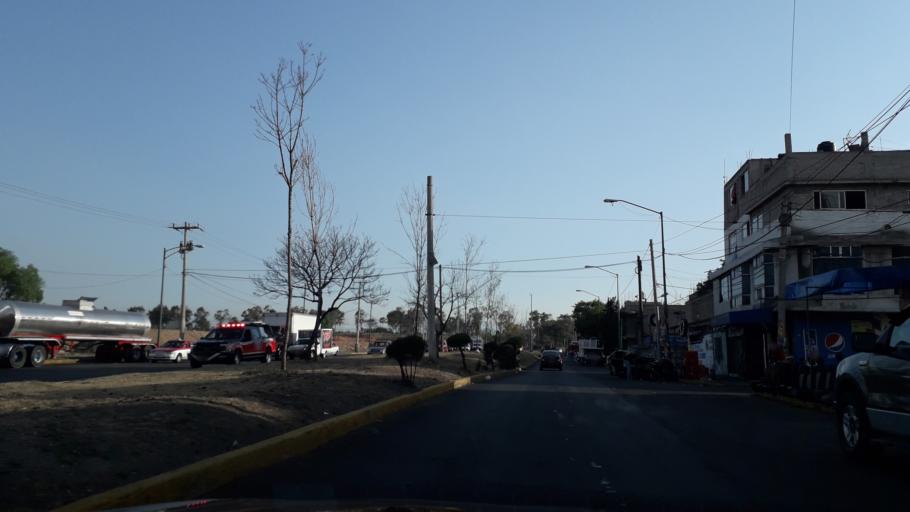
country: MX
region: Mexico City
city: Iztapalapa
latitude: 19.3716
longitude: -99.0459
